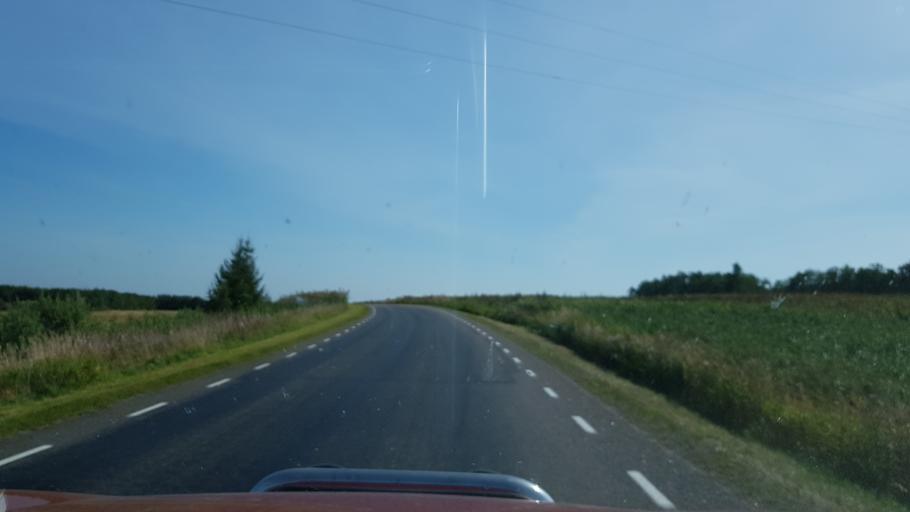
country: EE
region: Viljandimaa
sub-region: Viiratsi vald
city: Viiratsi
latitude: 58.5089
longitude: 25.6729
